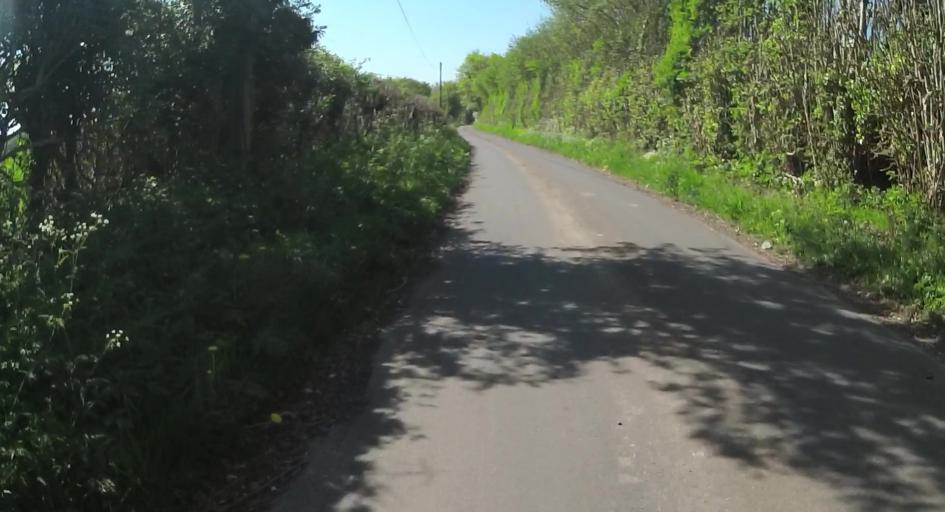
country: GB
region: England
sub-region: Hampshire
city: Four Marks
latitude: 51.1545
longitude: -1.0271
